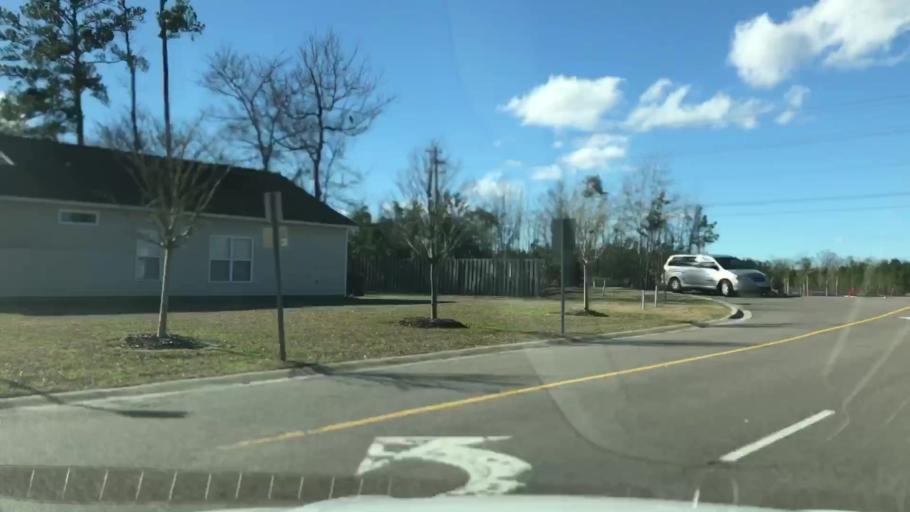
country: US
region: South Carolina
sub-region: Dorchester County
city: Summerville
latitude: 33.0897
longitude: -80.1982
